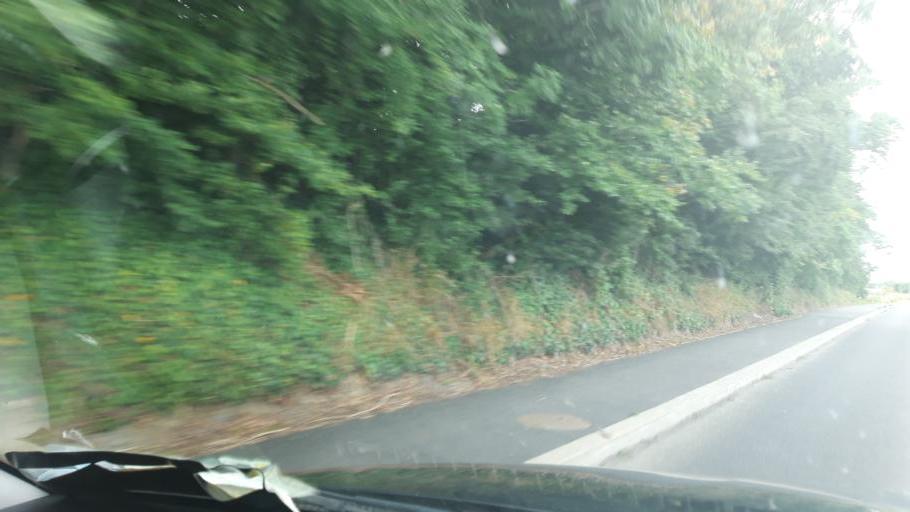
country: IE
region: Leinster
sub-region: Kilkenny
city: Kilkenny
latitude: 52.6369
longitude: -7.2715
